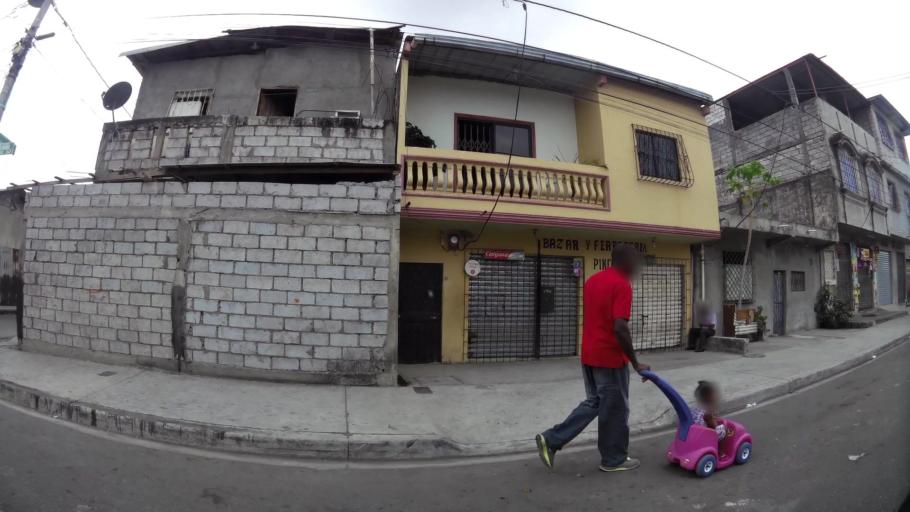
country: EC
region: Guayas
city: Guayaquil
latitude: -2.2319
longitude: -79.9126
